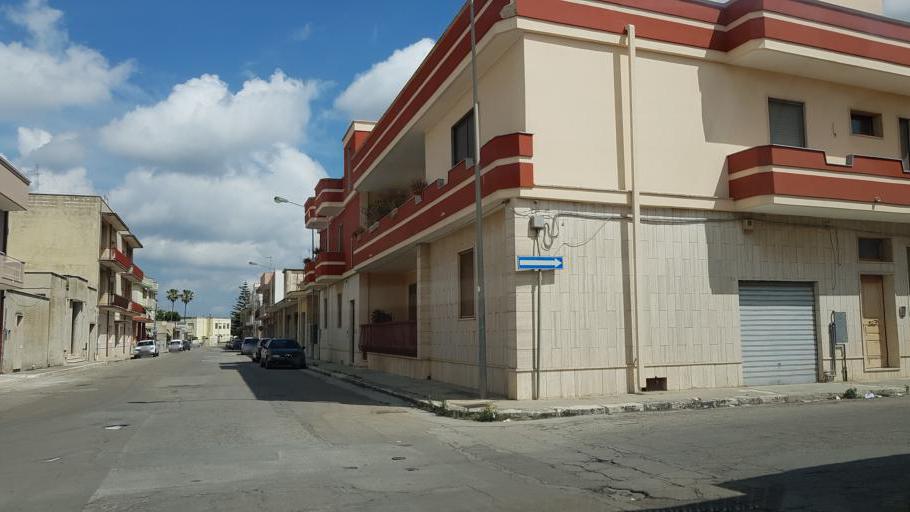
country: IT
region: Apulia
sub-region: Provincia di Brindisi
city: Mesagne
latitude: 40.5547
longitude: 17.8170
